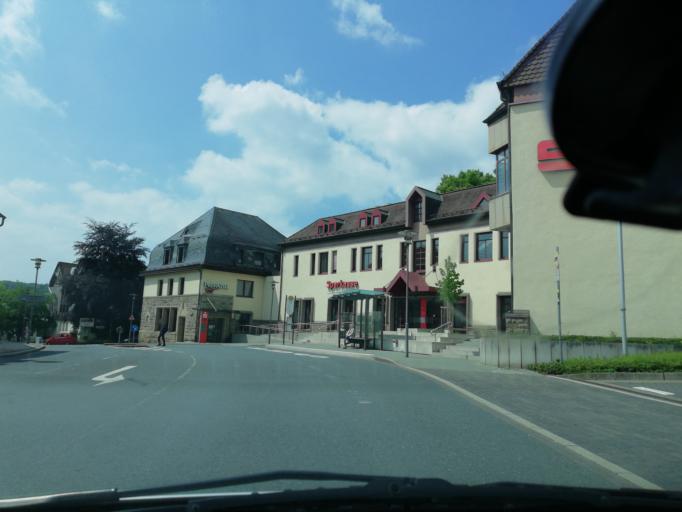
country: DE
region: North Rhine-Westphalia
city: Herdecke
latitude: 51.4007
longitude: 7.4320
